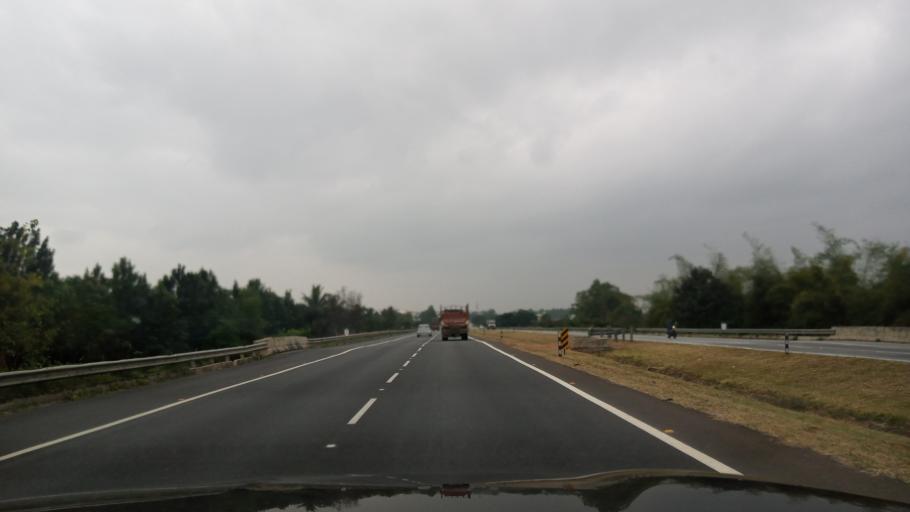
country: IN
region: Karnataka
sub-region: Bangalore Rural
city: Nelamangala
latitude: 13.0044
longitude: 77.4744
